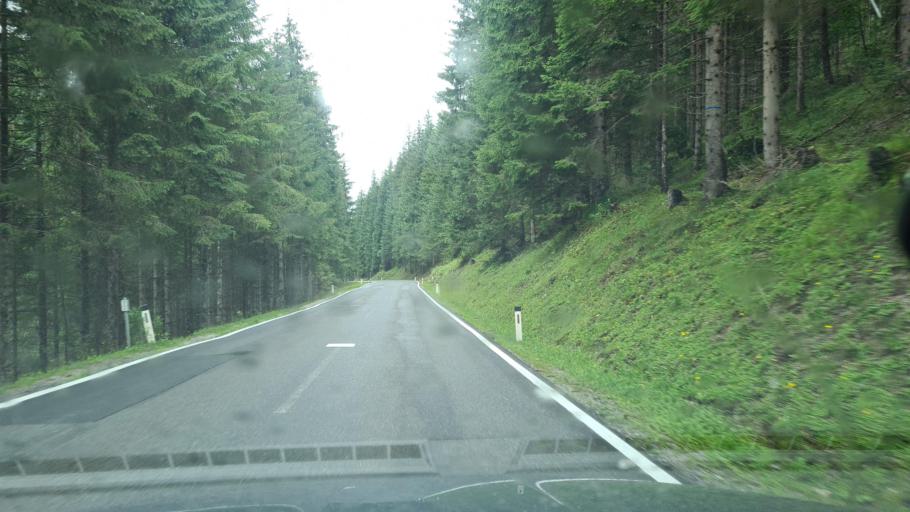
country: AT
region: Salzburg
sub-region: Politischer Bezirk Sankt Johann im Pongau
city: Untertauern
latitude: 47.3191
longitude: 13.4473
